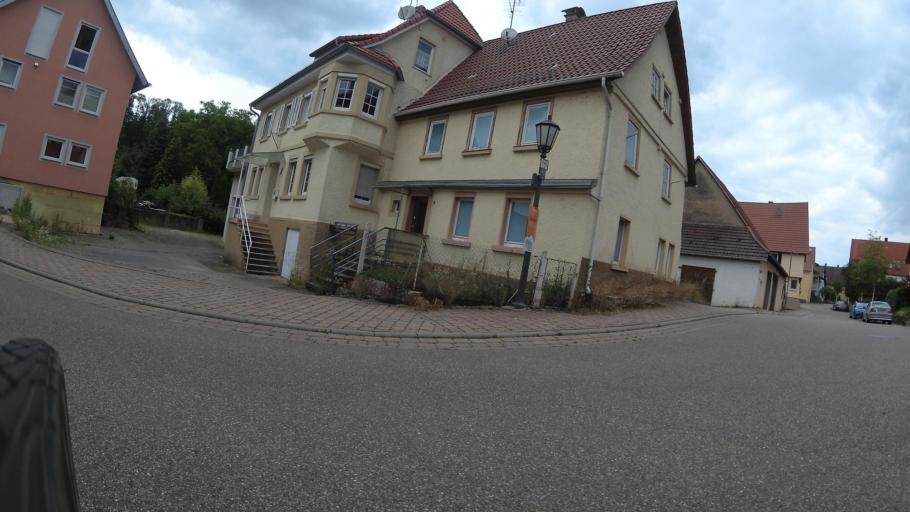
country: DE
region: Baden-Wuerttemberg
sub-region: Regierungsbezirk Stuttgart
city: Oedheim
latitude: 49.2687
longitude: 9.2213
